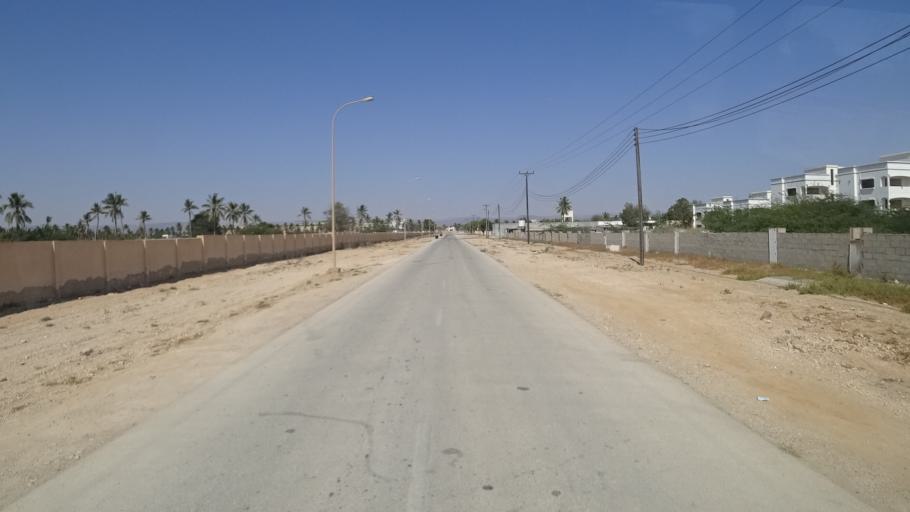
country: OM
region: Zufar
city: Salalah
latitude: 17.0264
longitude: 54.1666
